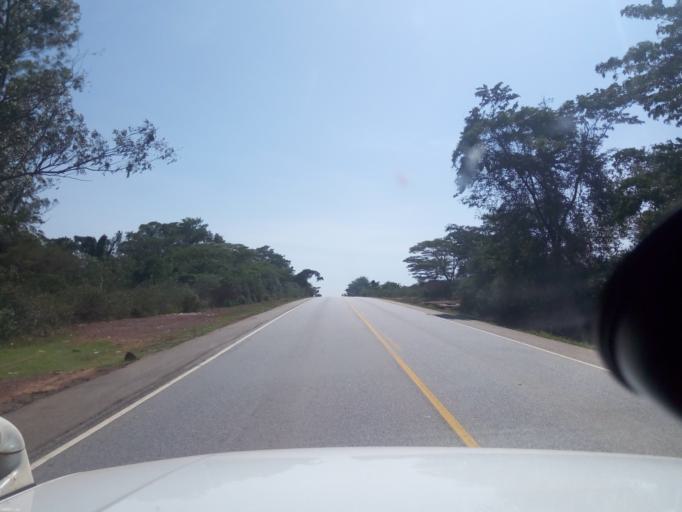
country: UG
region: Eastern Region
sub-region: Busia District
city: Busia
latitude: 0.5429
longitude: 34.0130
